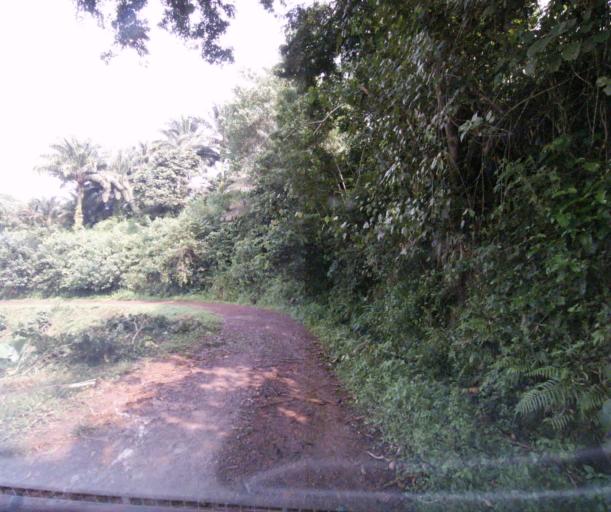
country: CM
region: Littoral
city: Melong
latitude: 5.0605
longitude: 9.9742
